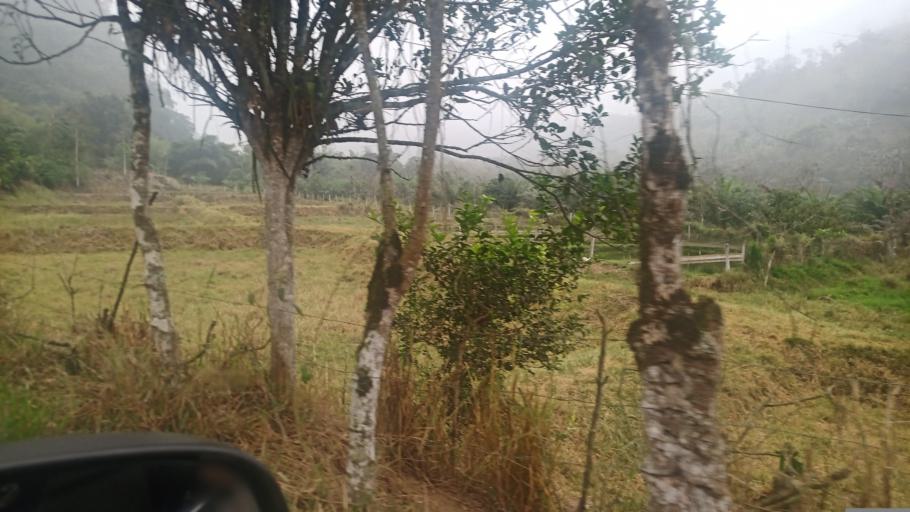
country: EC
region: Santo Domingo de los Tsachilas
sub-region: Canton Santo Domingo de los Colorados
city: Santo Domingo de los Colorados
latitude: -0.2795
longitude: -79.0694
